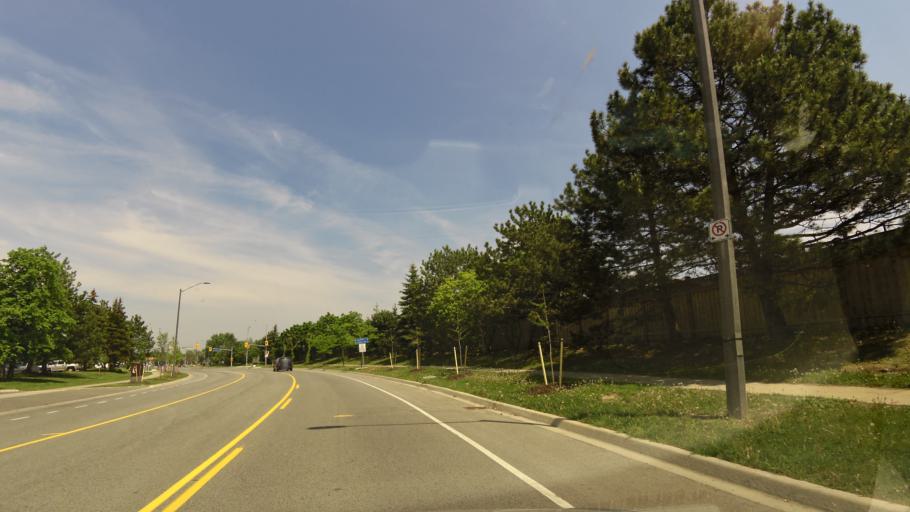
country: CA
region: Ontario
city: Mississauga
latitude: 43.5372
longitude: -79.7083
